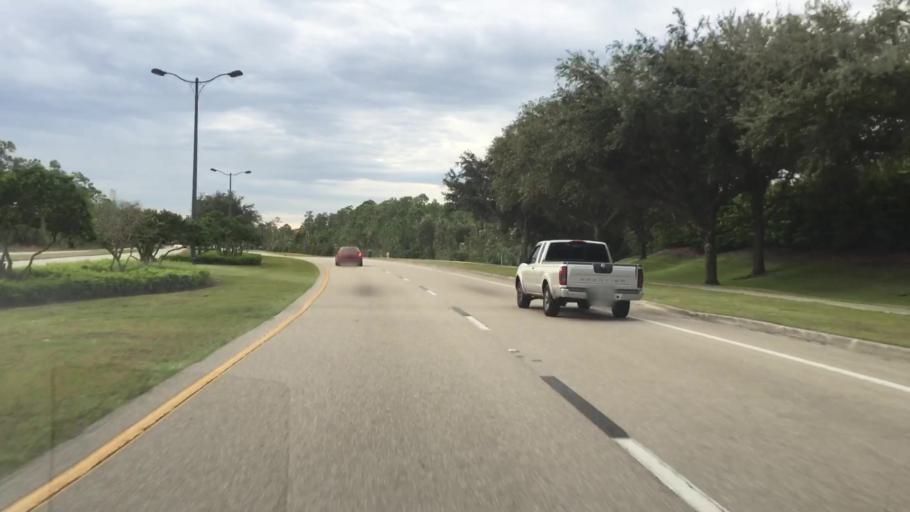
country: US
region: Florida
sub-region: Lee County
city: Three Oaks
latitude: 26.4649
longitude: -81.7858
